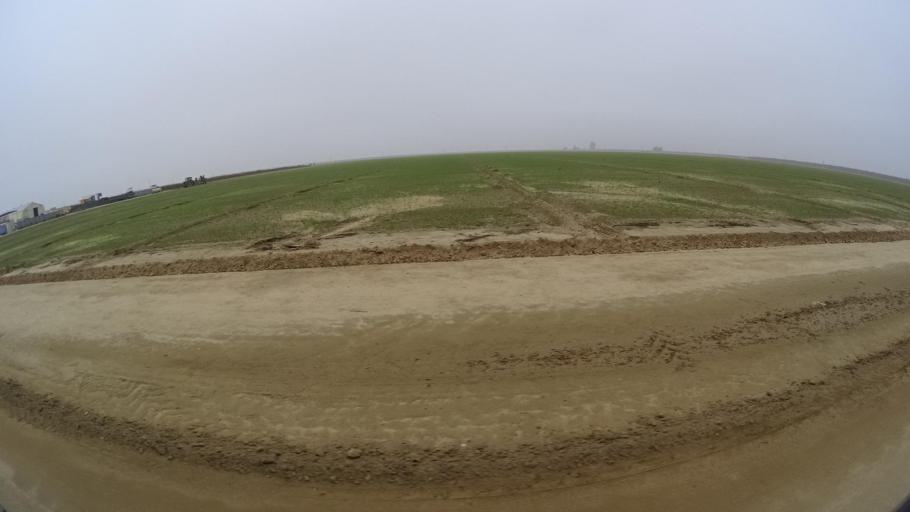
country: US
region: California
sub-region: Kern County
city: Lost Hills
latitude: 35.5865
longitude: -119.5333
